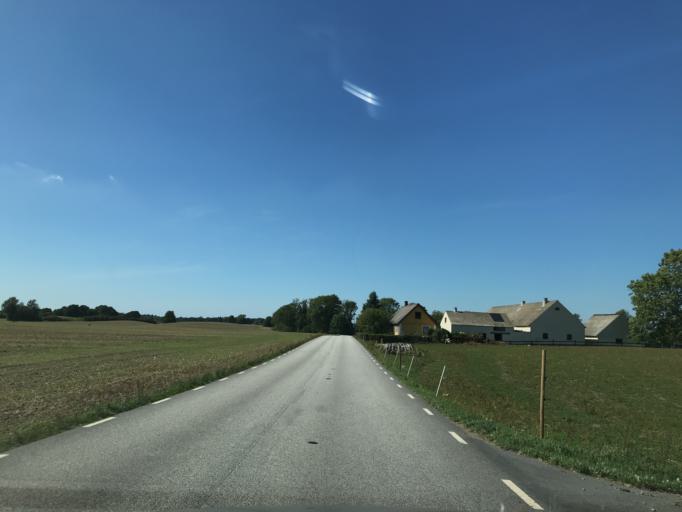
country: SE
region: Skane
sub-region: Tomelilla Kommun
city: Tomelilla
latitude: 55.6464
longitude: 13.9729
